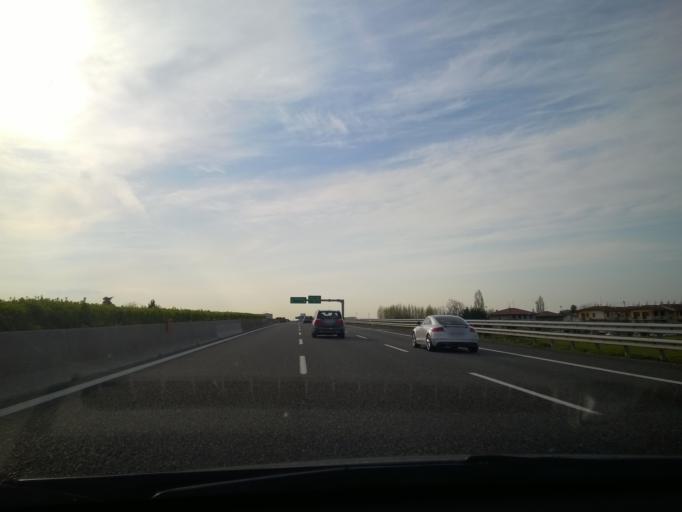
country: IT
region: Emilia-Romagna
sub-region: Forli-Cesena
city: Gatteo-Sant'Angelo
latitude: 44.1178
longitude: 12.4024
